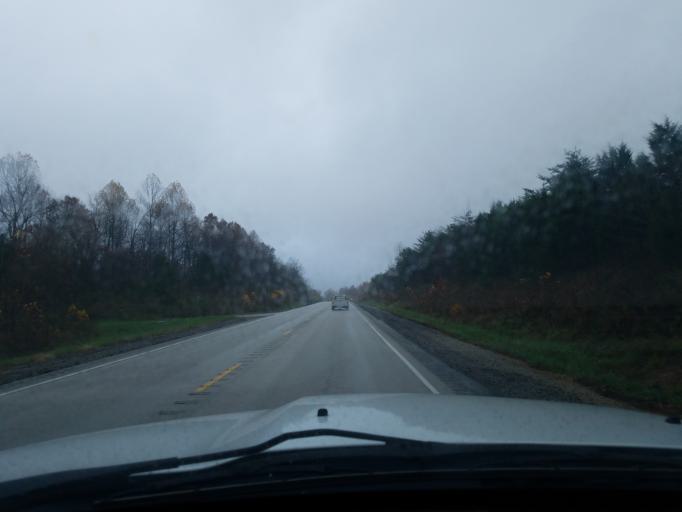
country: US
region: Kentucky
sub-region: Larue County
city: Hodgenville
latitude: 37.4729
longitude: -85.6070
